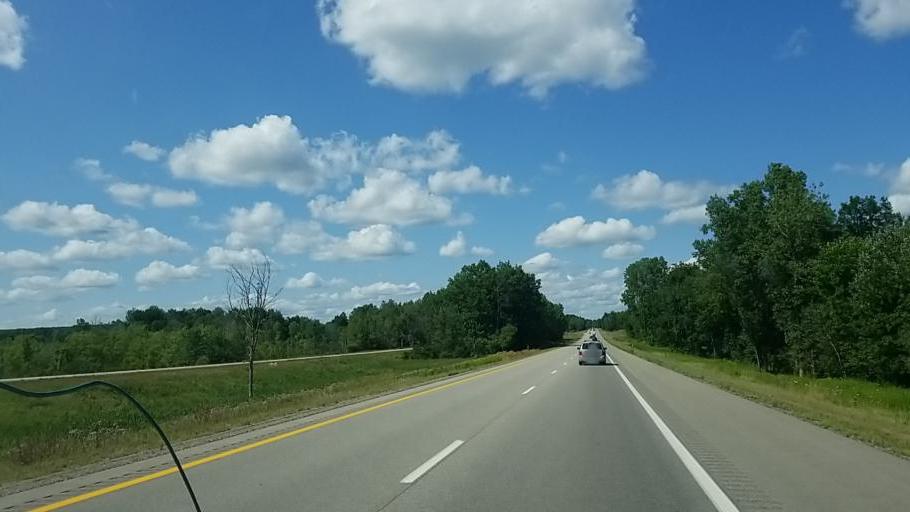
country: US
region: Michigan
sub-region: Montcalm County
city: Howard City
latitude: 43.5349
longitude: -85.4860
